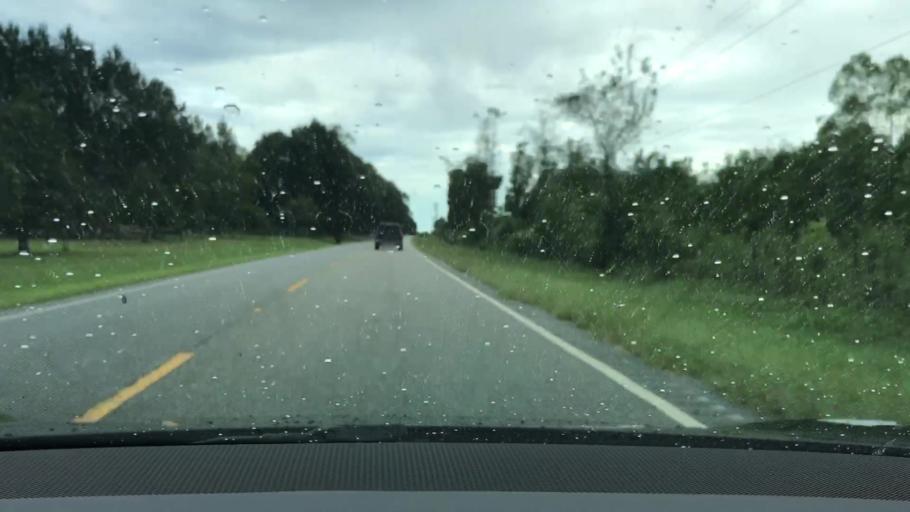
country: US
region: Alabama
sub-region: Geneva County
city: Samson
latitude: 31.0823
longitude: -86.1063
